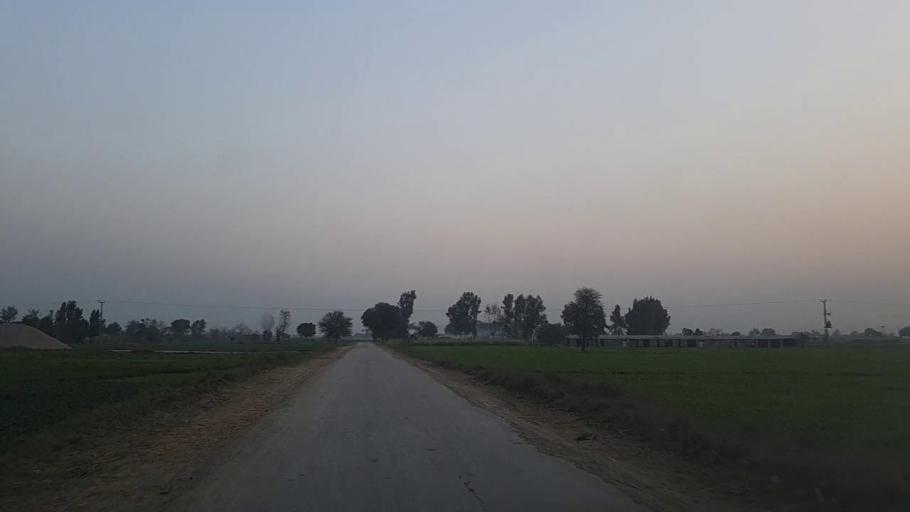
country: PK
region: Sindh
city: Naushahro Firoz
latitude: 26.8665
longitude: 68.0473
